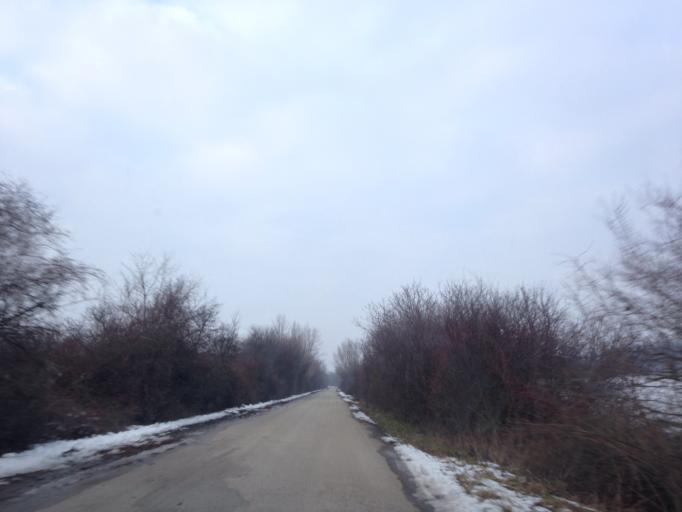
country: SK
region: Nitriansky
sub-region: Okres Nitra
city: Vrable
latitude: 48.0884
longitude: 18.3695
